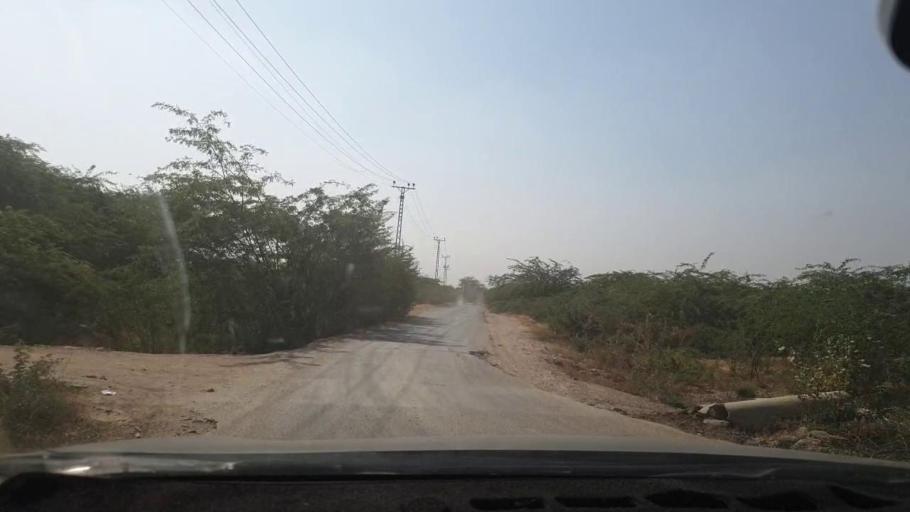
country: PK
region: Sindh
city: Malir Cantonment
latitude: 25.0974
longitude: 67.1891
